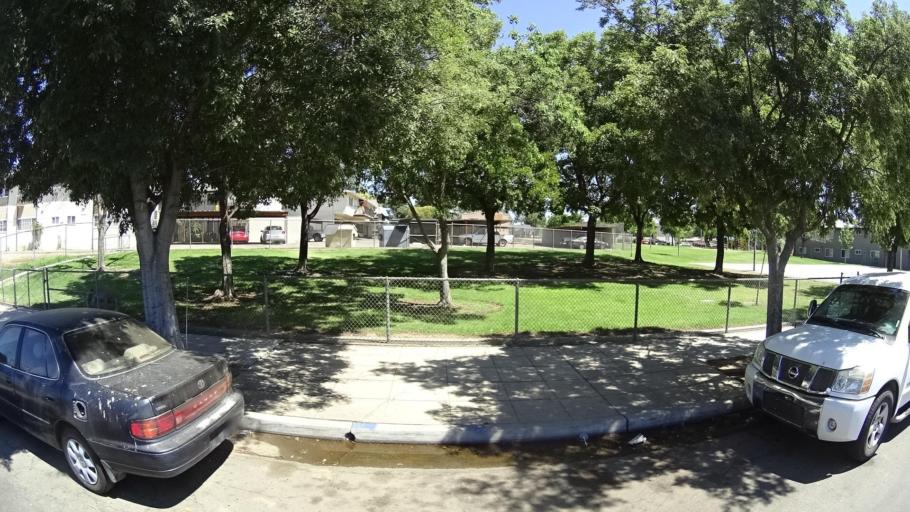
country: US
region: California
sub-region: Fresno County
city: Fresno
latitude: 36.7887
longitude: -119.7869
